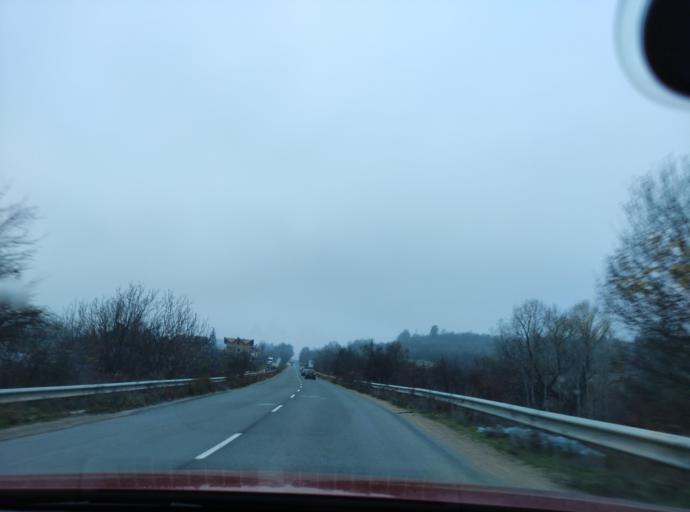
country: BG
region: Lovech
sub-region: Obshtina Yablanitsa
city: Yablanitsa
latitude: 43.0225
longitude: 24.0938
